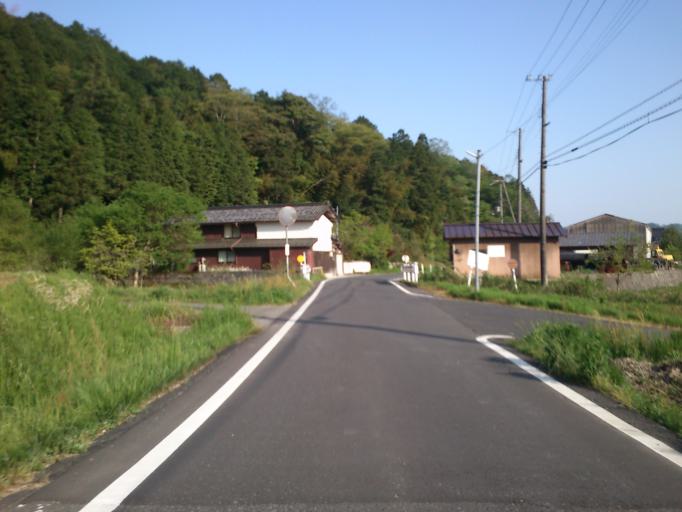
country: JP
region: Kyoto
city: Miyazu
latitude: 35.6110
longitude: 135.1348
